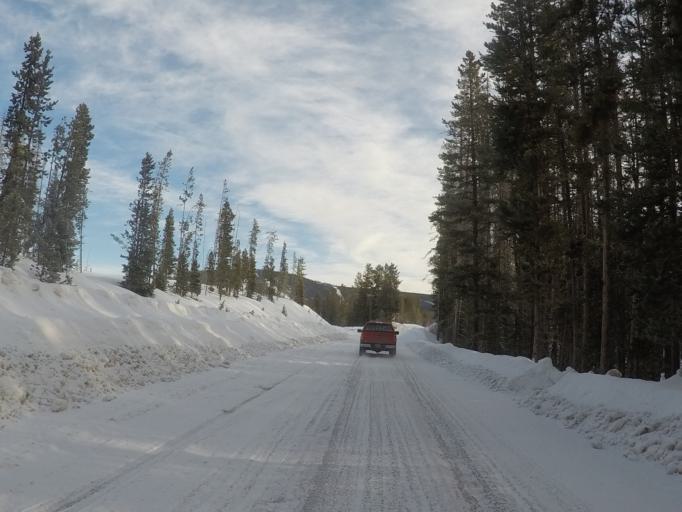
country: US
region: Montana
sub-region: Granite County
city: Philipsburg
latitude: 46.2261
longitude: -113.2506
